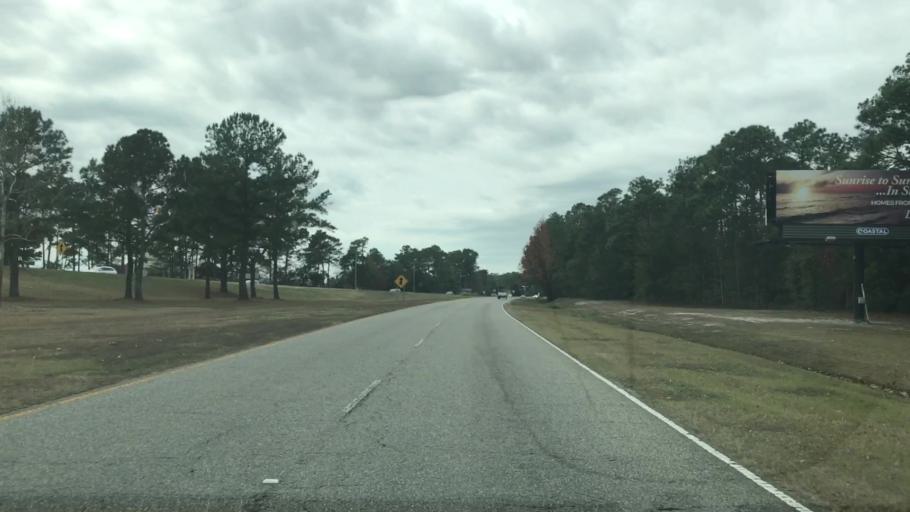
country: US
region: South Carolina
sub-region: Horry County
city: Myrtle Beach
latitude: 33.7676
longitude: -78.8069
